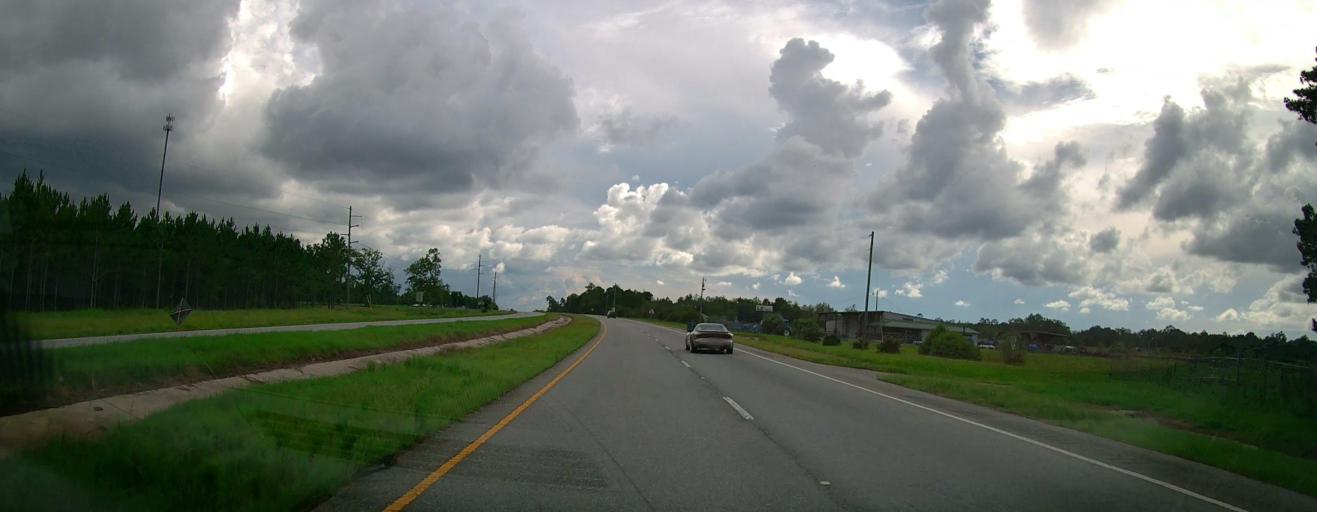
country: US
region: Georgia
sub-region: Pierce County
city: Blackshear
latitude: 31.4345
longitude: -82.0872
